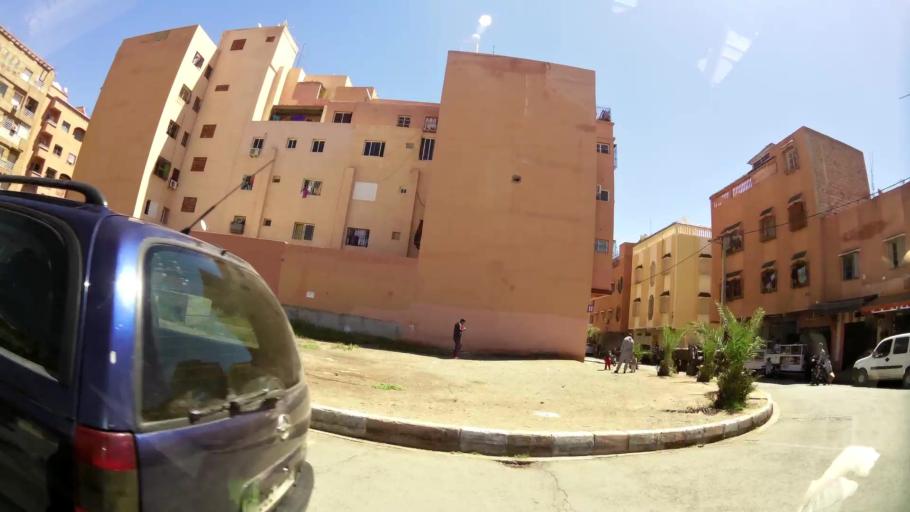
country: MA
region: Marrakech-Tensift-Al Haouz
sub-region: Marrakech
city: Marrakesh
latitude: 31.6333
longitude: -8.0607
